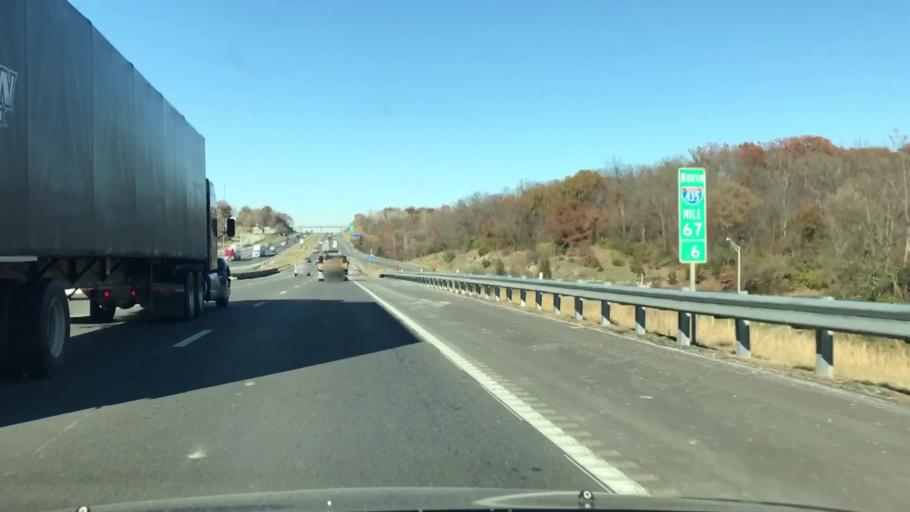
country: US
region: Missouri
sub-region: Jackson County
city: Raytown
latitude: 38.9945
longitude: -94.5024
